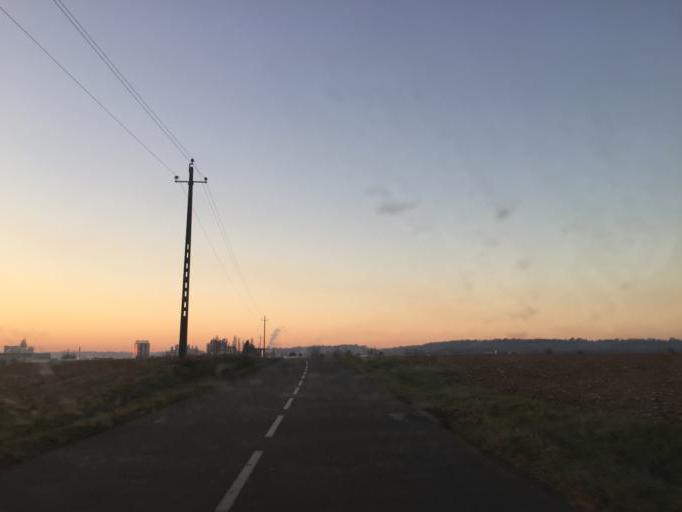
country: FR
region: Rhone-Alpes
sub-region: Departement de l'Ain
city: Balan
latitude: 45.8437
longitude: 5.1087
